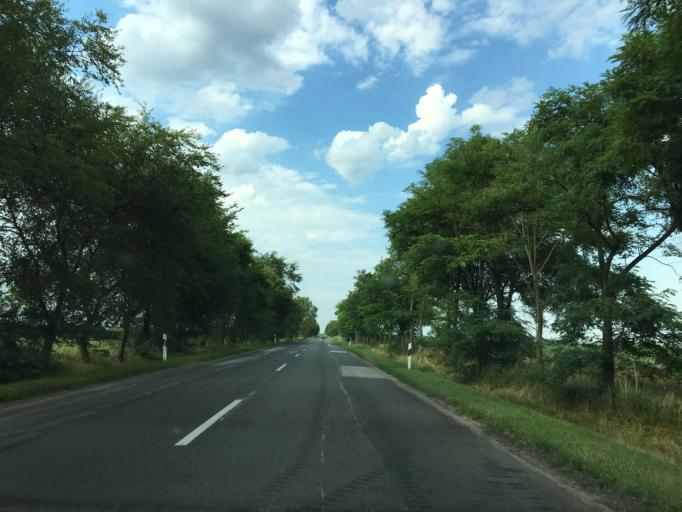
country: HU
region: Bacs-Kiskun
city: Batya
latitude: 46.4386
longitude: 18.9491
